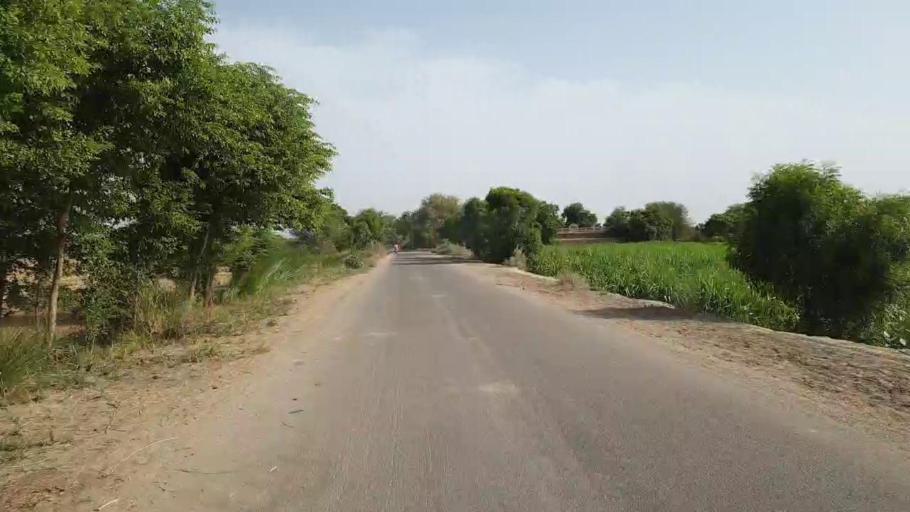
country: PK
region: Sindh
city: Sakrand
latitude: 26.2538
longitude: 68.2847
